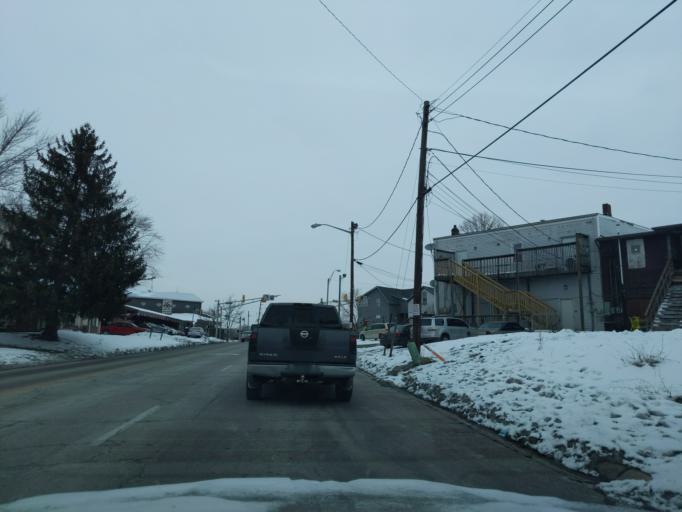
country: US
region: Indiana
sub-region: Tippecanoe County
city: Lafayette
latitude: 40.4152
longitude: -86.8772
